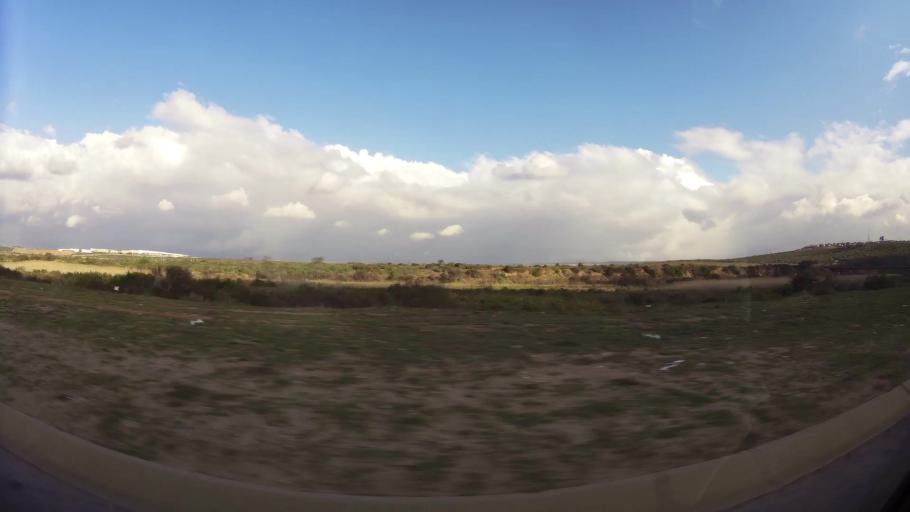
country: ZA
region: Eastern Cape
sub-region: Nelson Mandela Bay Metropolitan Municipality
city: Uitenhage
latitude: -33.7910
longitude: 25.4116
